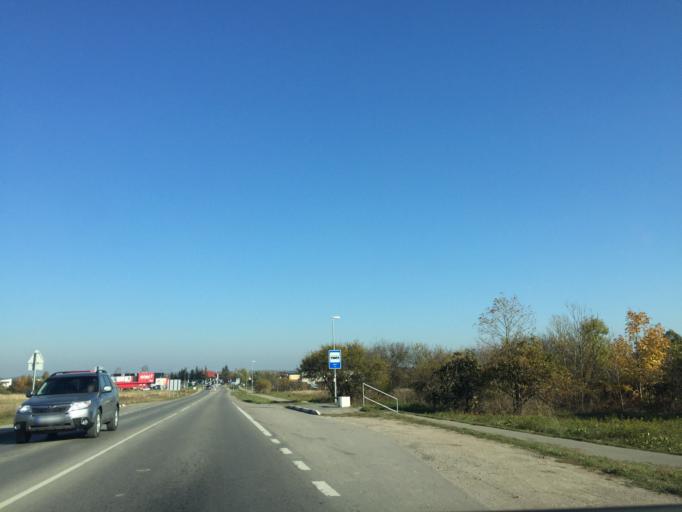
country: LT
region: Klaipedos apskritis
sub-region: Klaipeda
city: Klaipeda
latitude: 55.7338
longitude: 21.1891
